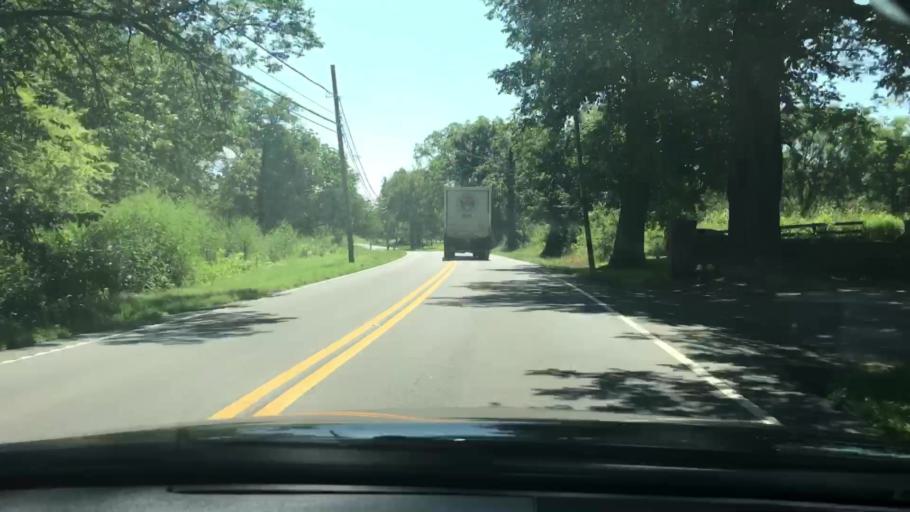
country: US
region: Tennessee
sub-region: Sumner County
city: Gallatin
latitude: 36.4085
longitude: -86.5004
